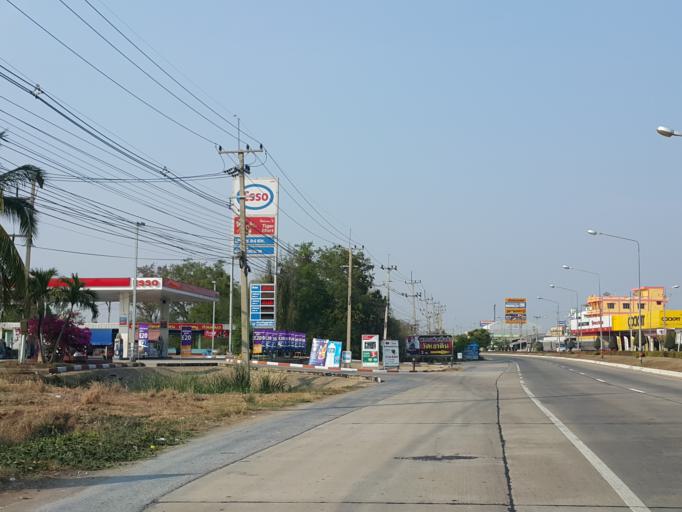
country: TH
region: Suphan Buri
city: Doembang Nangbuat
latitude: 14.8032
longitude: 100.1129
